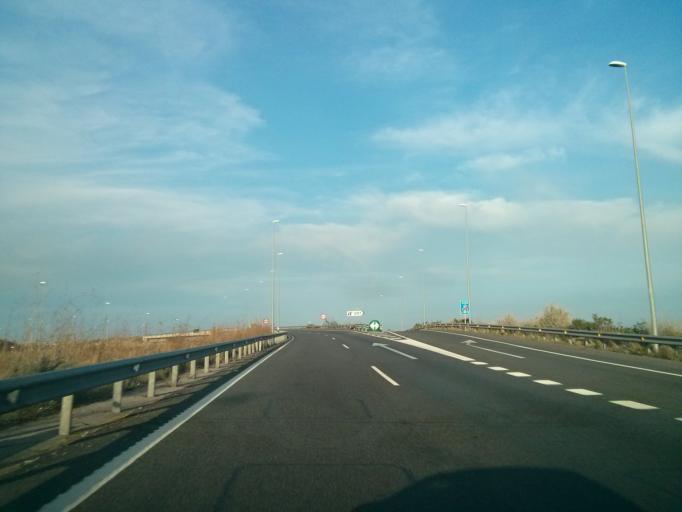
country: ES
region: Valencia
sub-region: Provincia de Valencia
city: Sagunto
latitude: 39.7003
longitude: -0.2677
